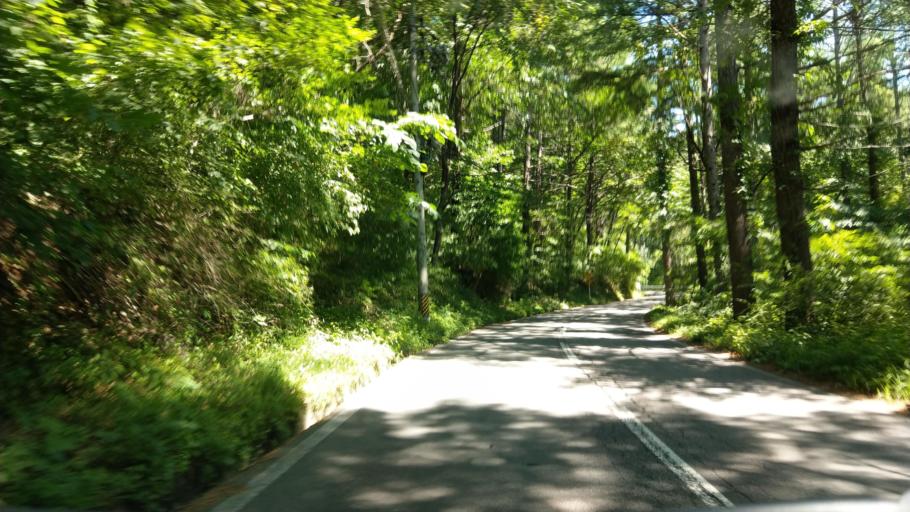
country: JP
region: Nagano
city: Komoro
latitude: 36.3702
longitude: 138.4607
